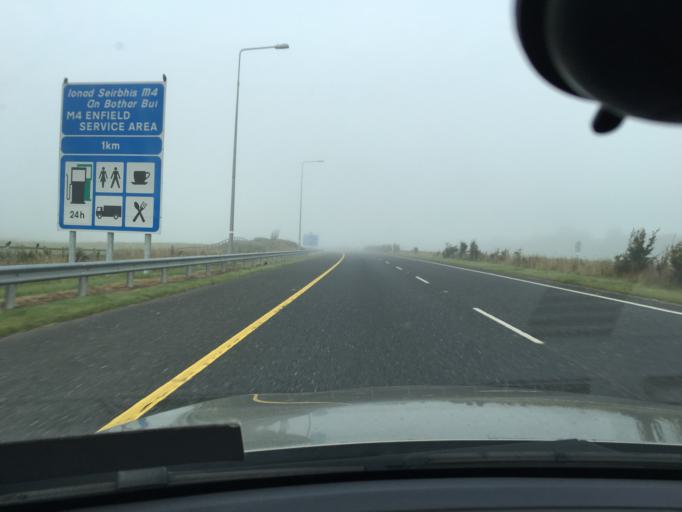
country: IE
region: Leinster
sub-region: An Mhi
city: Enfield
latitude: 53.4123
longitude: -6.8579
